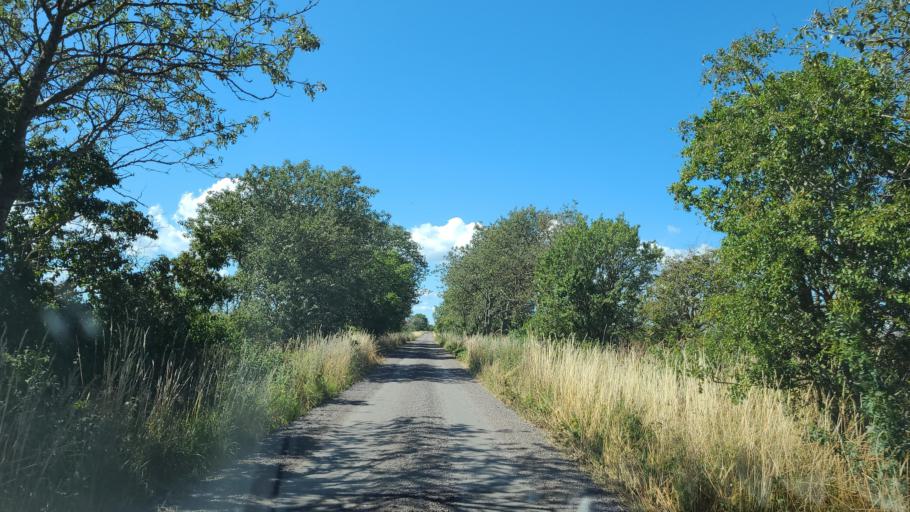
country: SE
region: Kalmar
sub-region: Morbylanga Kommun
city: Sodra Sandby
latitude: 56.7118
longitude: 16.7167
